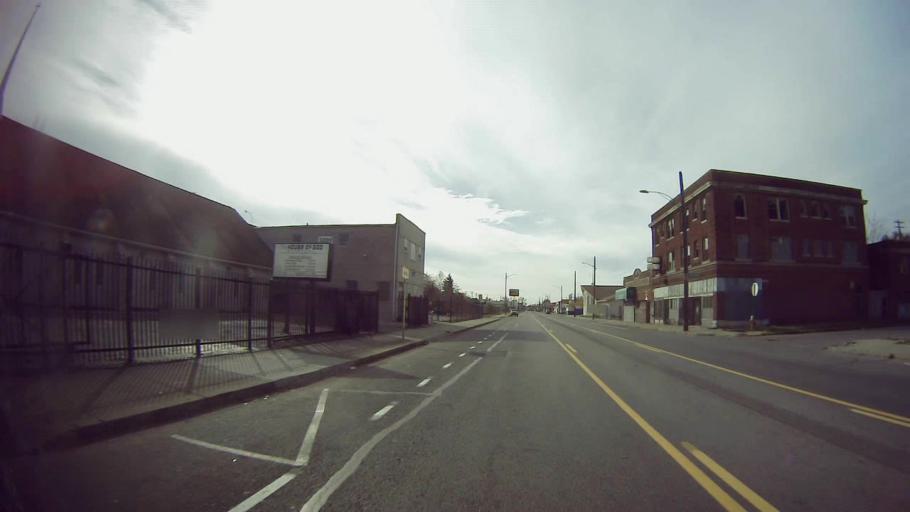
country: US
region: Michigan
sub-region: Wayne County
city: Highland Park
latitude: 42.3717
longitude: -83.1135
